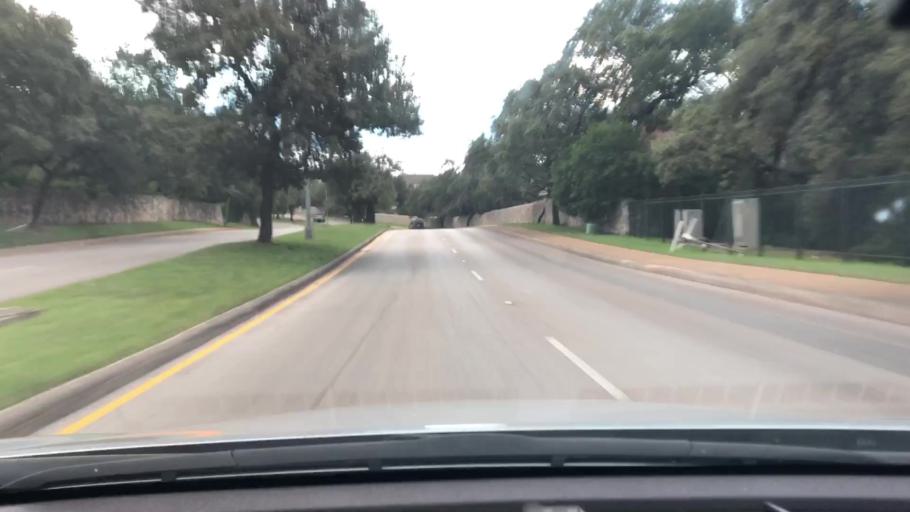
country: US
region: Texas
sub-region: Bexar County
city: Shavano Park
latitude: 29.5988
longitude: -98.5337
